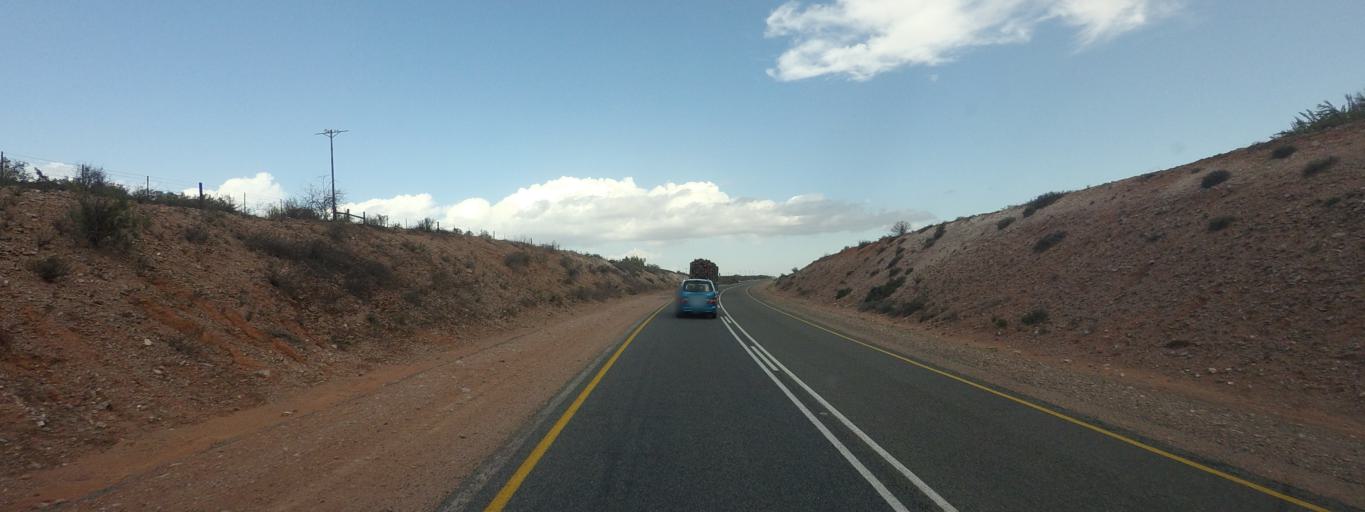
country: ZA
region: Western Cape
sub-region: Central Karoo District Municipality
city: Prince Albert
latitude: -33.5234
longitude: 21.7273
